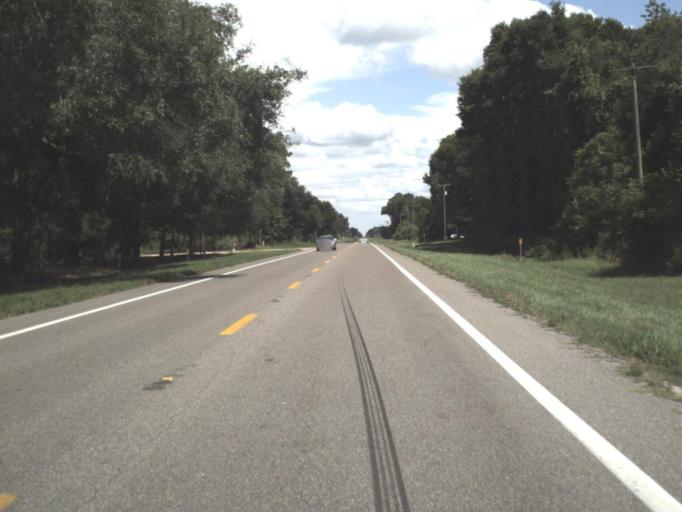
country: US
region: Florida
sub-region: Lafayette County
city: Mayo
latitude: 30.0464
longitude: -83.0805
